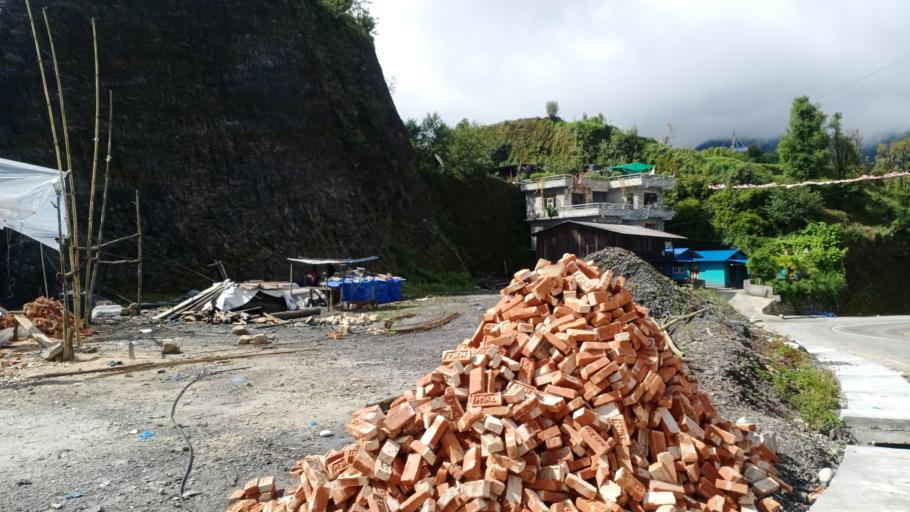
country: NP
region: Central Region
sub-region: Janakpur Zone
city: Ramechhap
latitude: 27.6316
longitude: 86.1793
